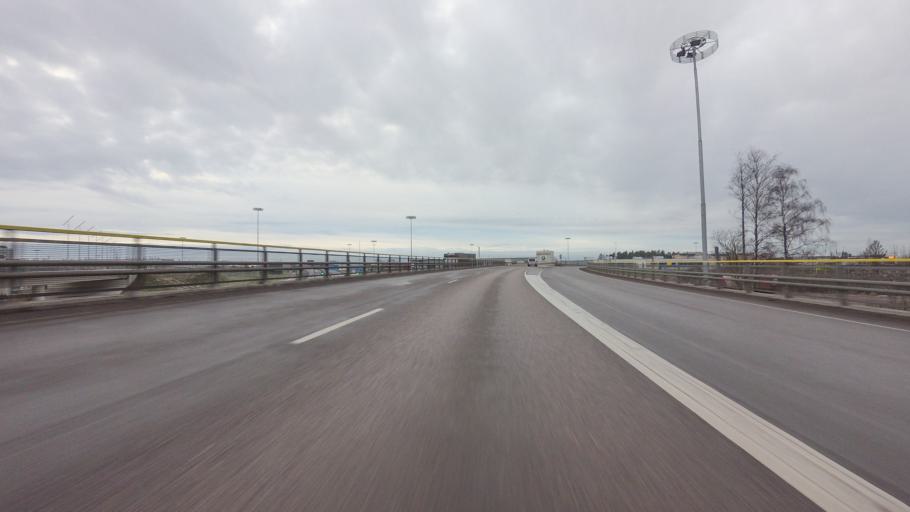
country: FI
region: Uusimaa
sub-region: Helsinki
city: Vantaa
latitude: 60.2973
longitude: 24.9582
